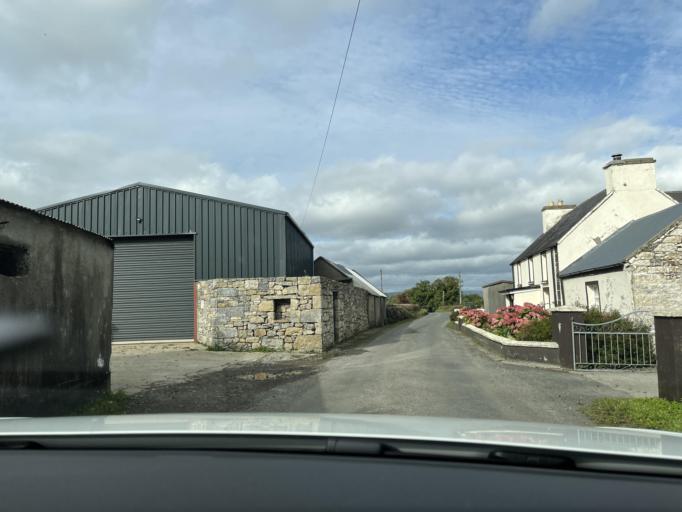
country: IE
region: Connaught
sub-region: County Leitrim
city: Carrick-on-Shannon
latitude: 53.9592
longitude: -8.0699
